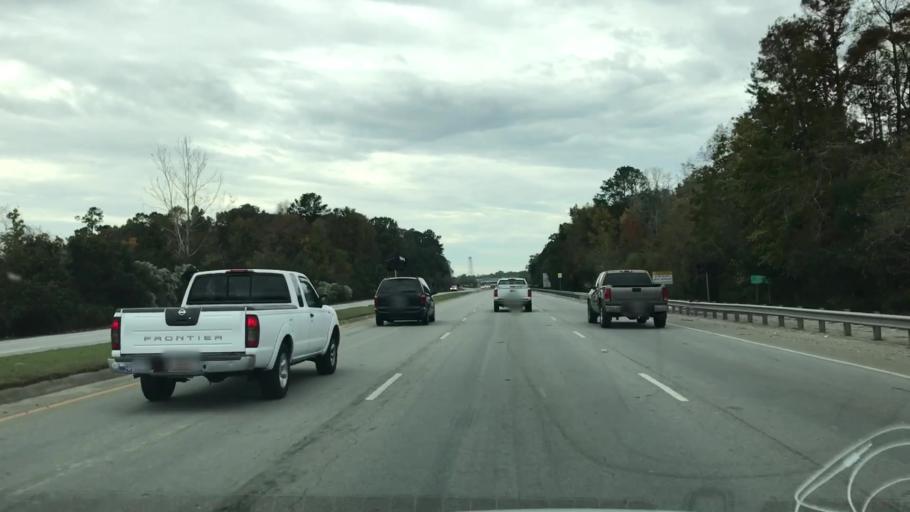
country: US
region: South Carolina
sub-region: Berkeley County
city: Goose Creek
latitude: 32.9839
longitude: -80.0420
